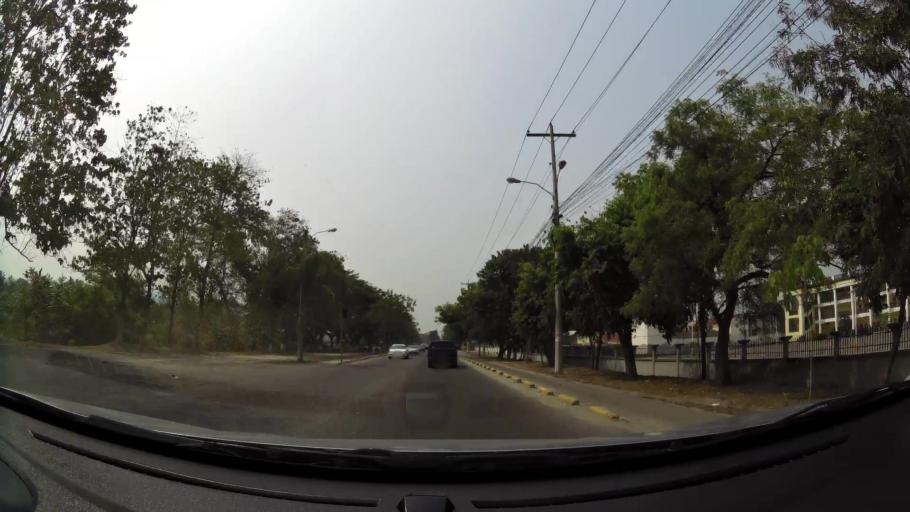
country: HN
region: Cortes
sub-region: San Pedro Sula
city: Pena Blanca
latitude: 15.5507
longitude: -88.0111
